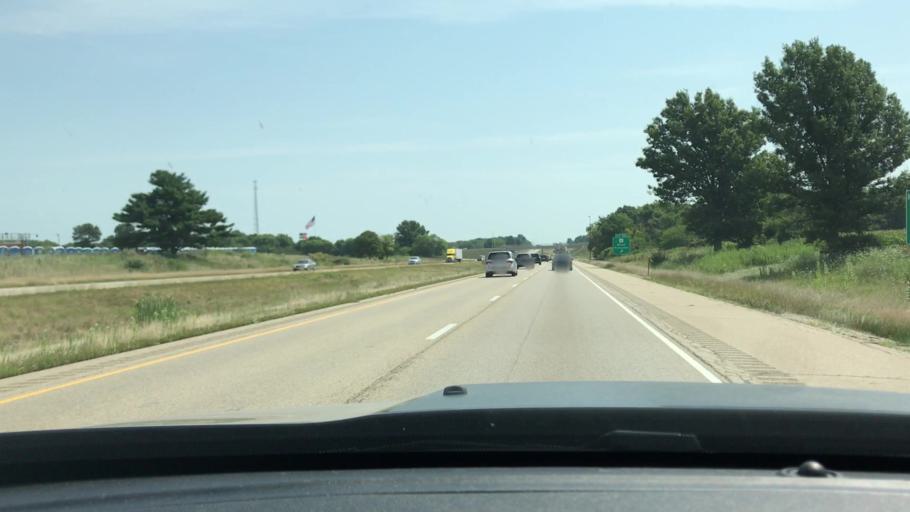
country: US
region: Illinois
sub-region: Bureau County
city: Princeton
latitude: 41.3982
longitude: -89.4783
